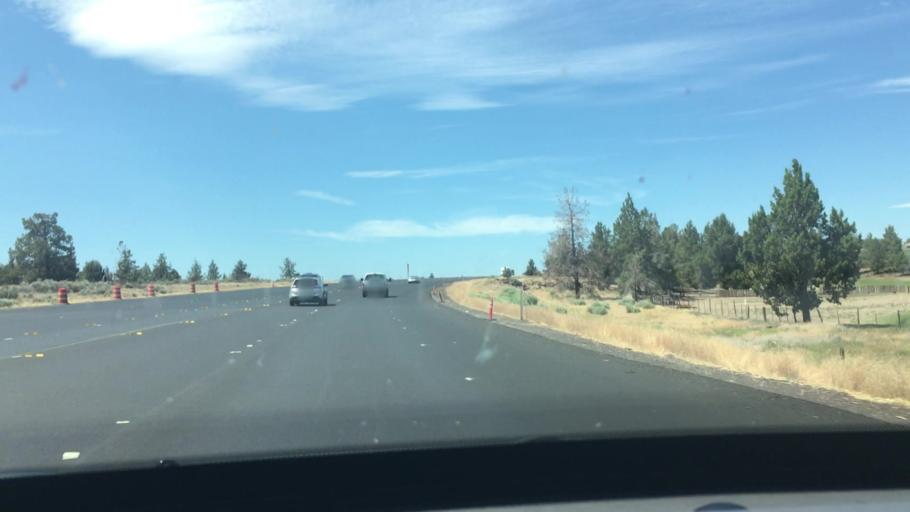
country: US
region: Oregon
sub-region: Deschutes County
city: Terrebonne
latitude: 44.3961
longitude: -121.1964
